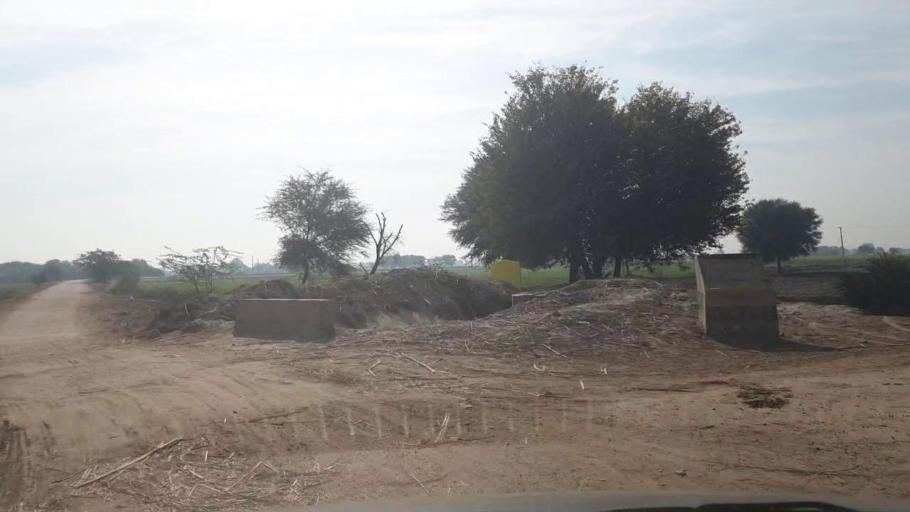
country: PK
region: Sindh
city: Shahpur Chakar
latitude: 26.1850
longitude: 68.5834
